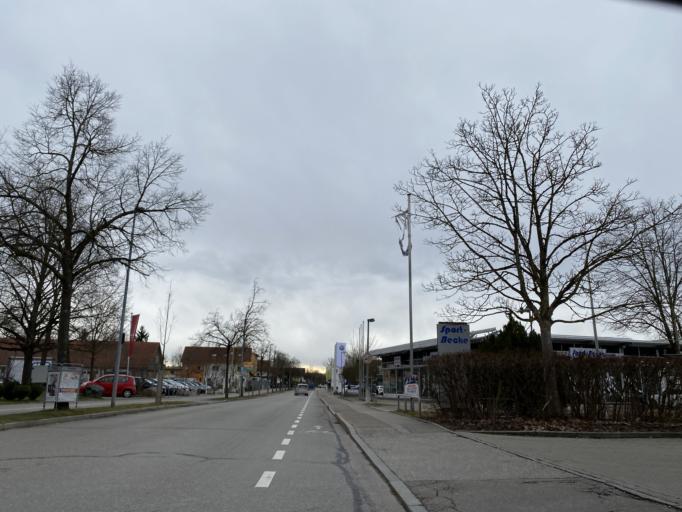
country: DE
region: Bavaria
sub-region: Upper Bavaria
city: Fuerstenfeldbruck
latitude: 48.1929
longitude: 11.2562
